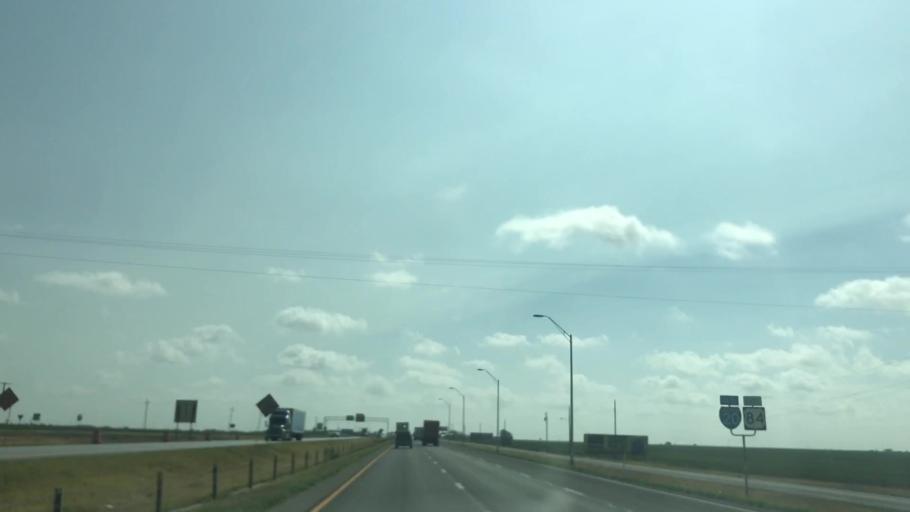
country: US
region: Texas
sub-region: Nolan County
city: Roscoe
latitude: 32.4477
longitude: -100.4979
